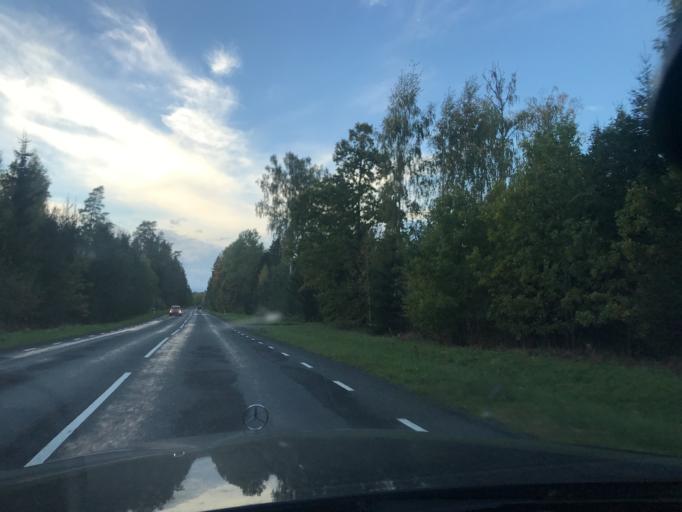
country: EE
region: Vorumaa
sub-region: Antsla vald
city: Vana-Antsla
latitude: 57.8748
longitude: 26.5884
